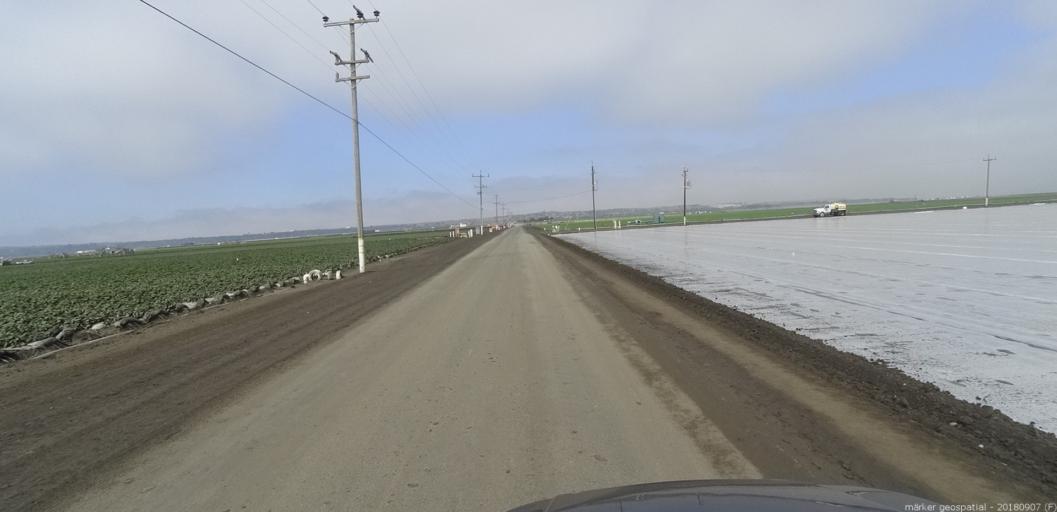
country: US
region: California
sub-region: Monterey County
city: Boronda
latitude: 36.6932
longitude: -121.7247
